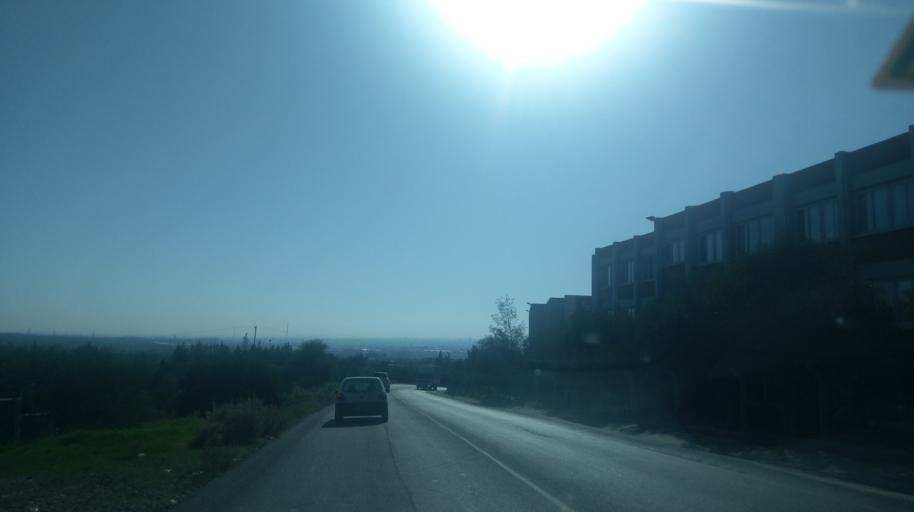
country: CY
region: Lefkosia
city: Nicosia
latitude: 35.2301
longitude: 33.3262
